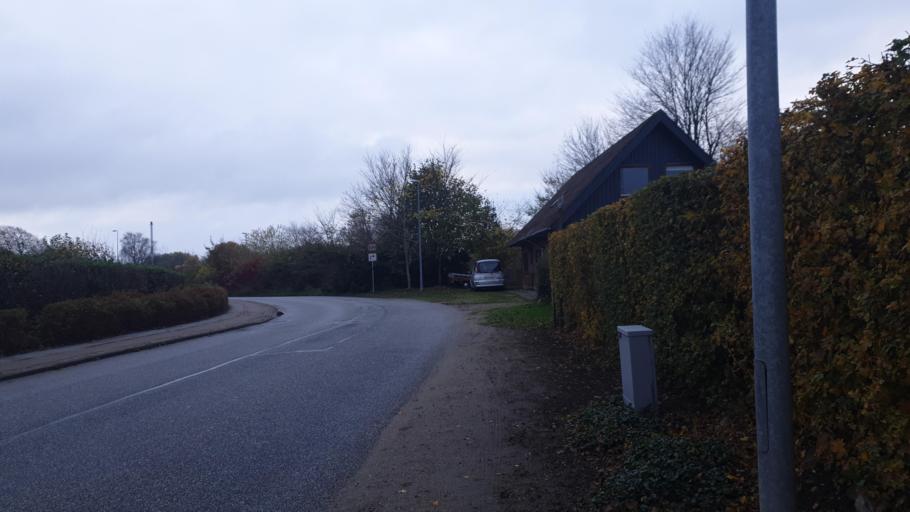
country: DK
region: Central Jutland
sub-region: Hedensted Kommune
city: Hedensted
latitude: 55.7633
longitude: 9.6993
